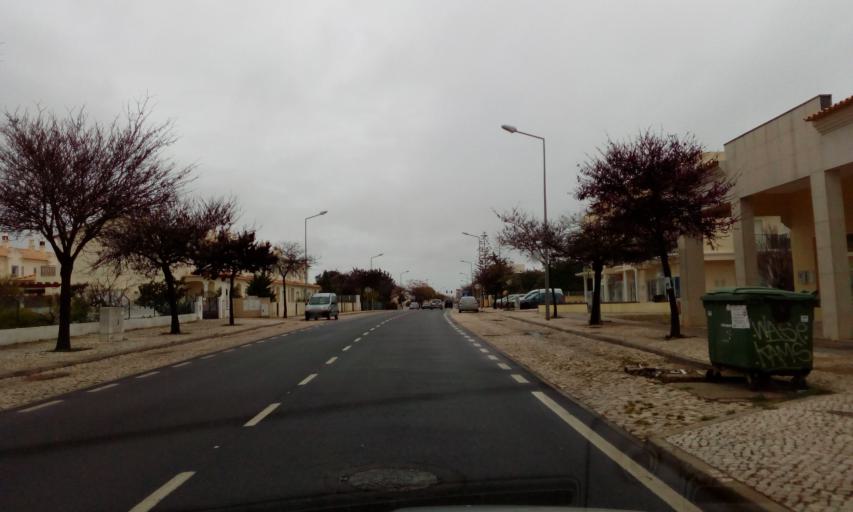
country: PT
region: Faro
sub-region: Albufeira
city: Ferreiras
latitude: 37.1249
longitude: -8.2294
